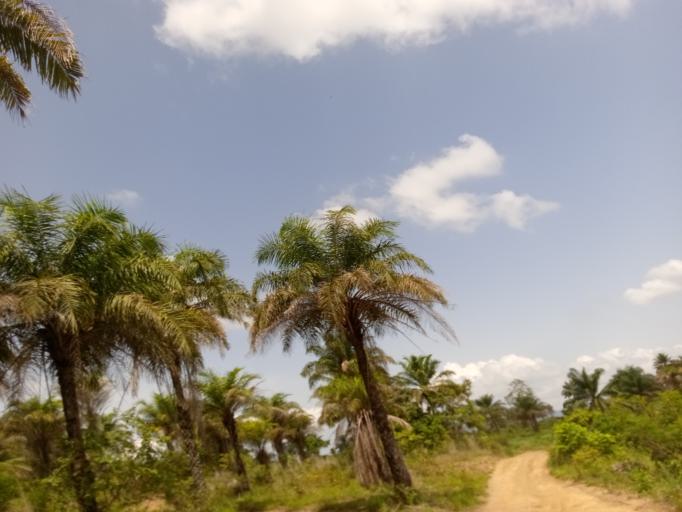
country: SL
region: Western Area
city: Waterloo
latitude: 8.3578
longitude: -13.0060
